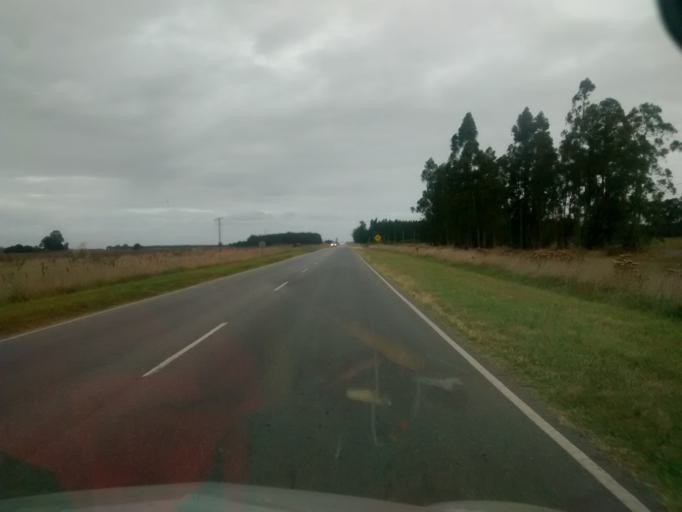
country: AR
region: Buenos Aires
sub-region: Partido de Loberia
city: Loberia
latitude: -38.2100
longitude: -58.7339
